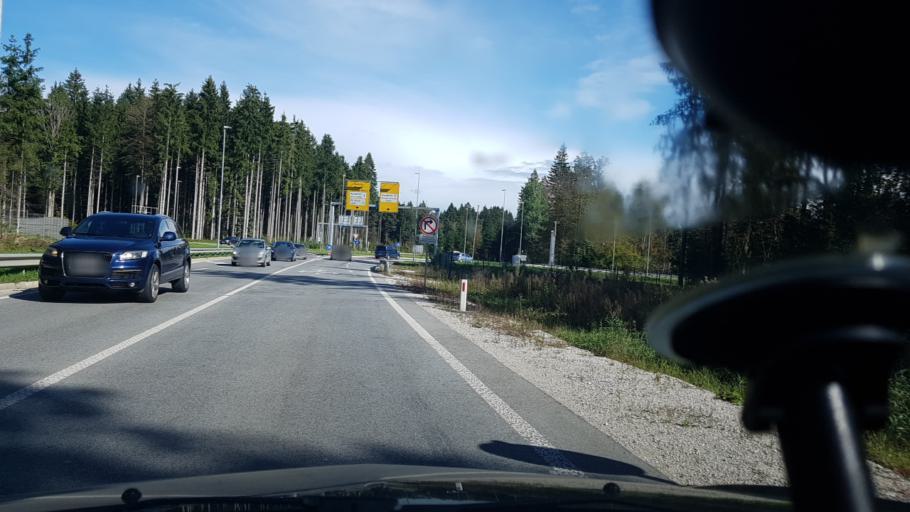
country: SI
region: Sencur
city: Sencur
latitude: 46.2357
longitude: 14.4498
